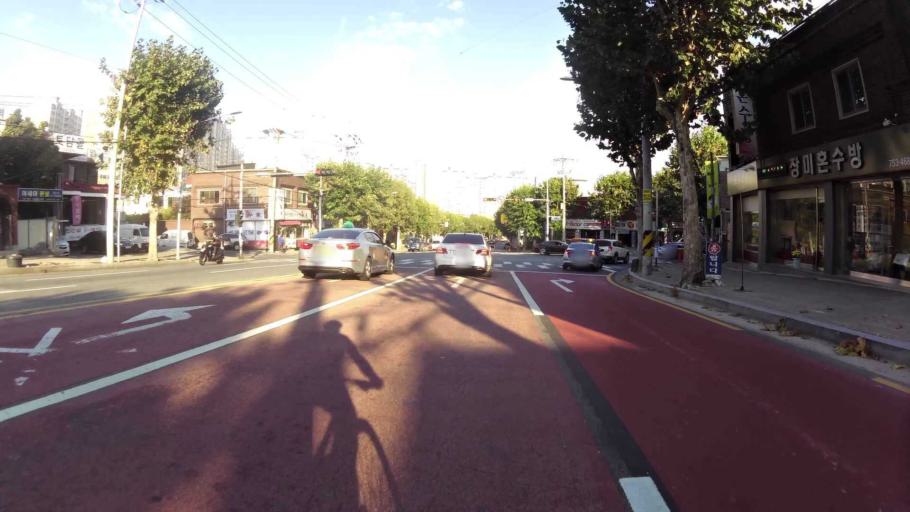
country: KR
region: Daegu
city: Daegu
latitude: 35.8672
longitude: 128.6331
